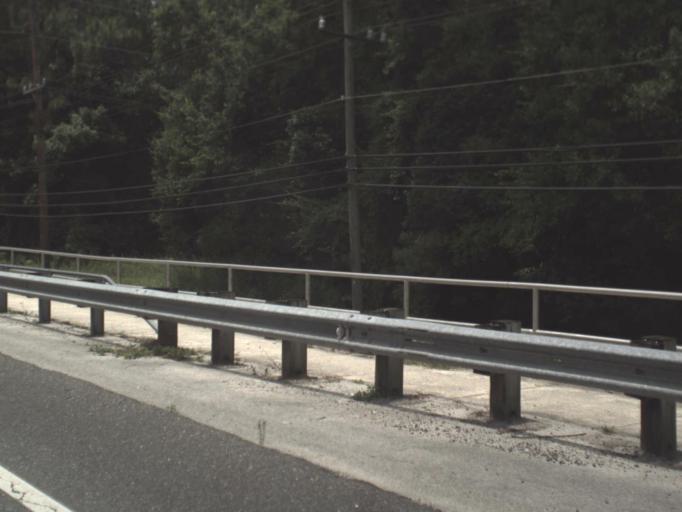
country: US
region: Florida
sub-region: Bradford County
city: Starke
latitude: 29.9389
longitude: -82.1062
